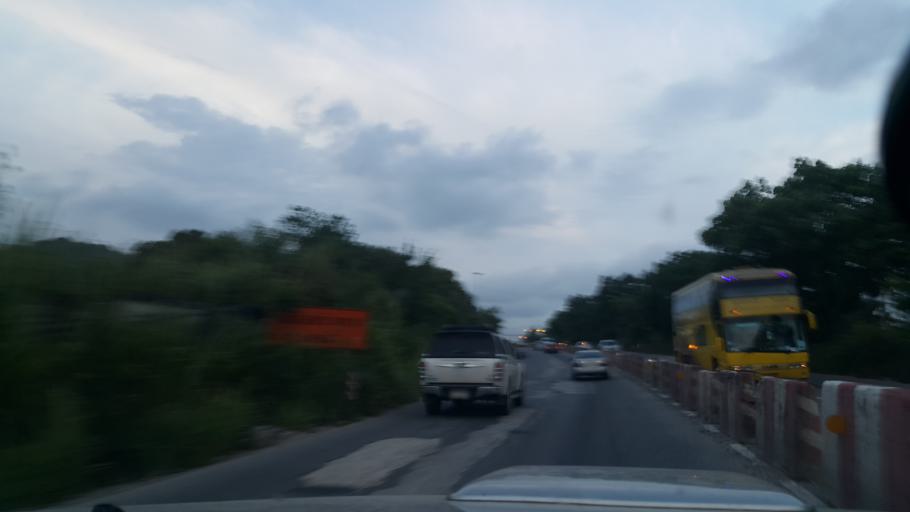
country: TH
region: Rayong
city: Ban Chang
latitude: 12.7089
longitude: 101.0250
